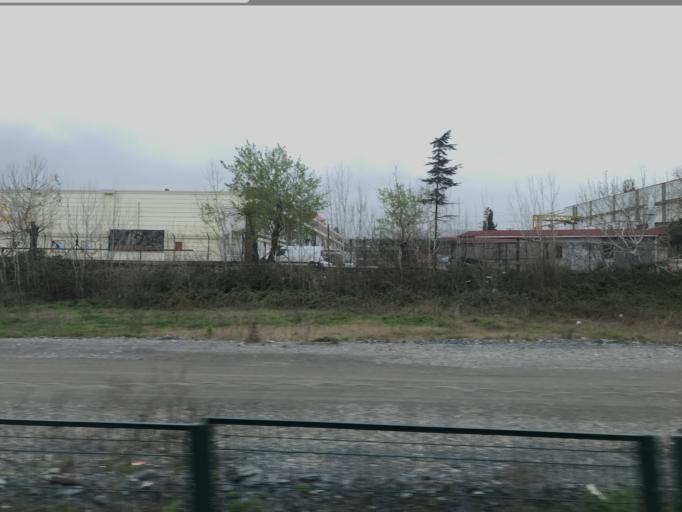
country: TR
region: Kocaeli
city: Darica
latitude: 40.7958
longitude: 29.3853
